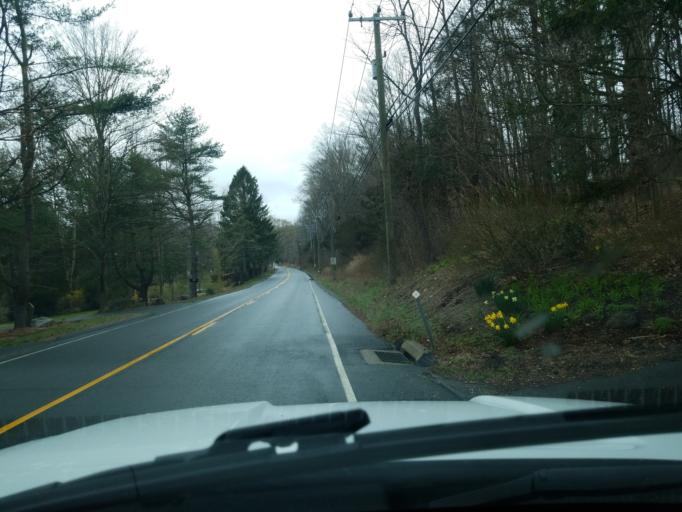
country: US
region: Connecticut
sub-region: New Haven County
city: Guilford
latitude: 41.3135
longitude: -72.6950
